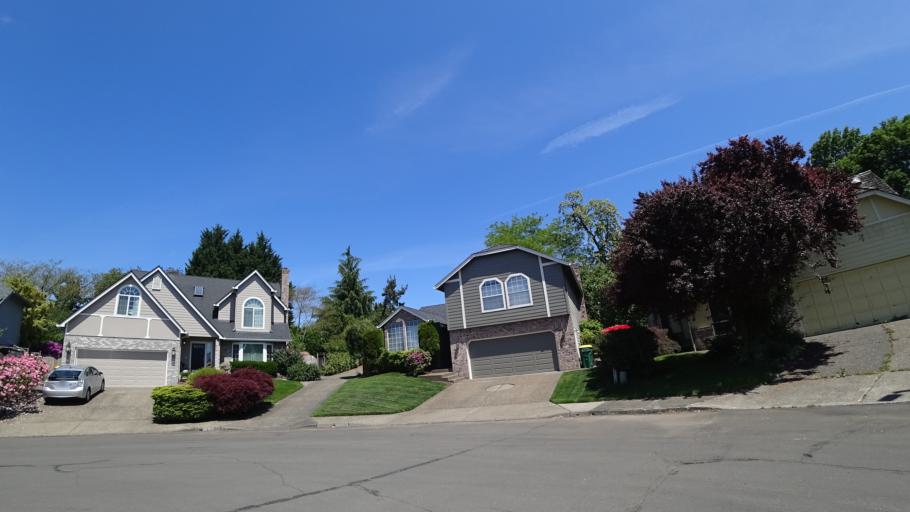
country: US
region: Oregon
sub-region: Washington County
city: Tigard
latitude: 45.4381
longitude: -122.8015
